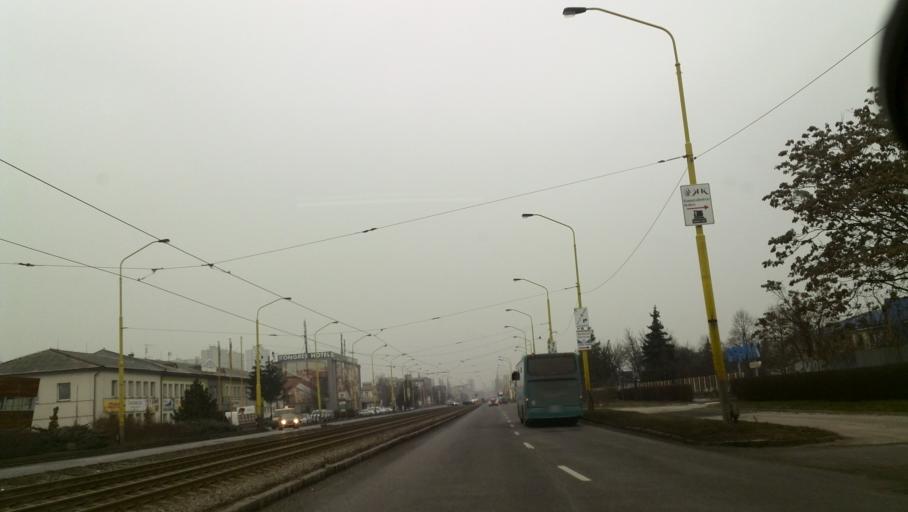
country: SK
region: Kosicky
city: Kosice
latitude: 48.6959
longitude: 21.2645
